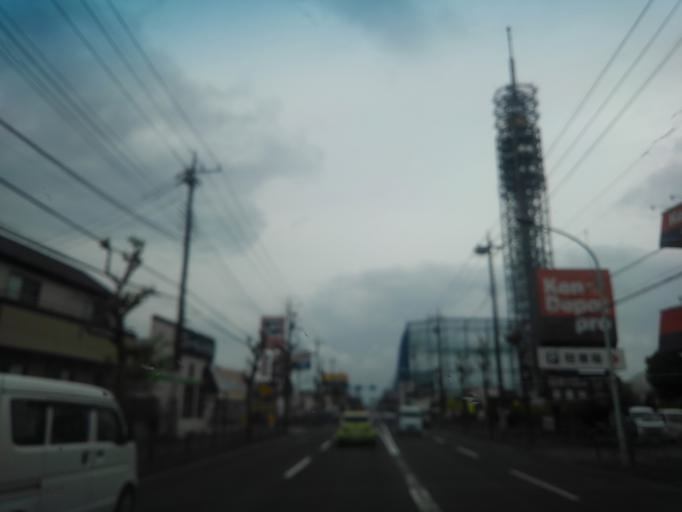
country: JP
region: Tokyo
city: Tanashicho
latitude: 35.7363
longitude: 139.5209
